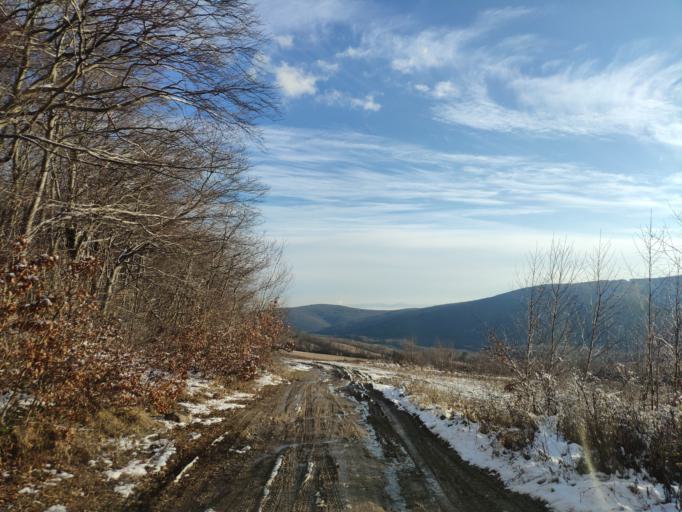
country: SK
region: Kosicky
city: Moldava nad Bodvou
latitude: 48.7415
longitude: 21.0849
